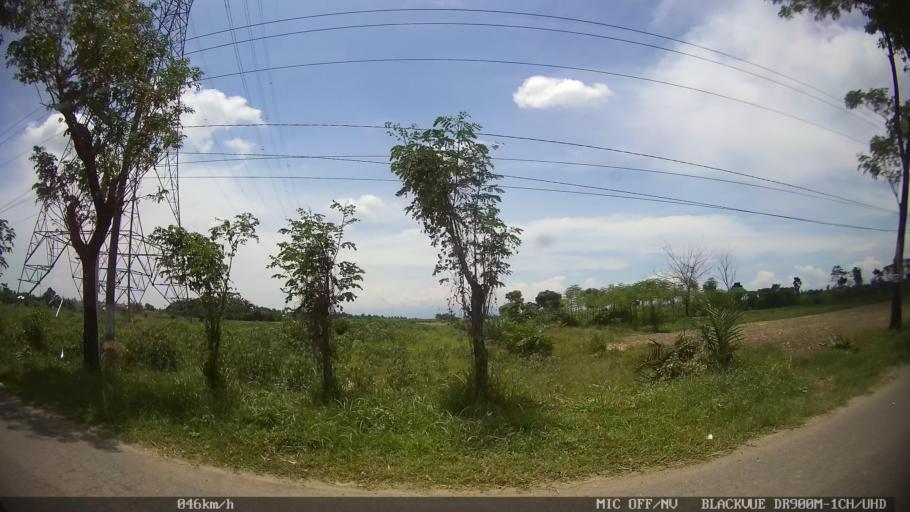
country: ID
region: North Sumatra
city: Binjai
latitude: 3.5909
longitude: 98.5130
